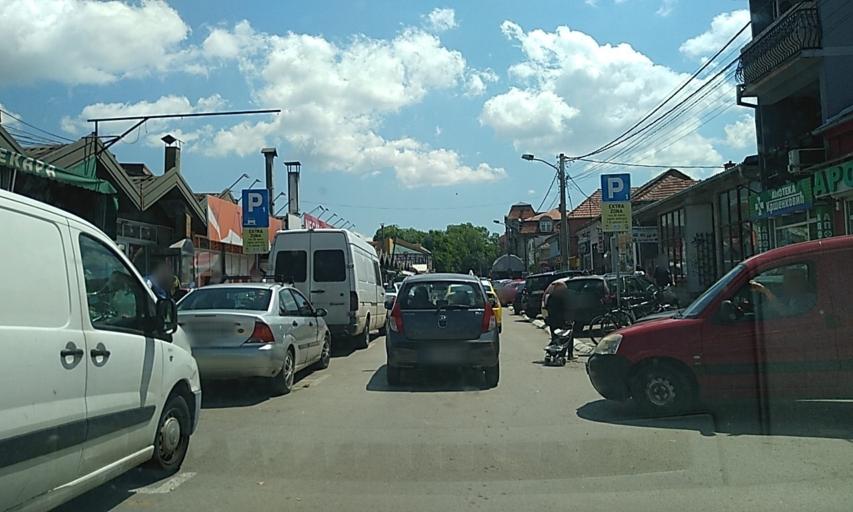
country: RS
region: Central Serbia
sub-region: Nisavski Okrug
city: Nis
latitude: 43.3243
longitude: 21.8918
